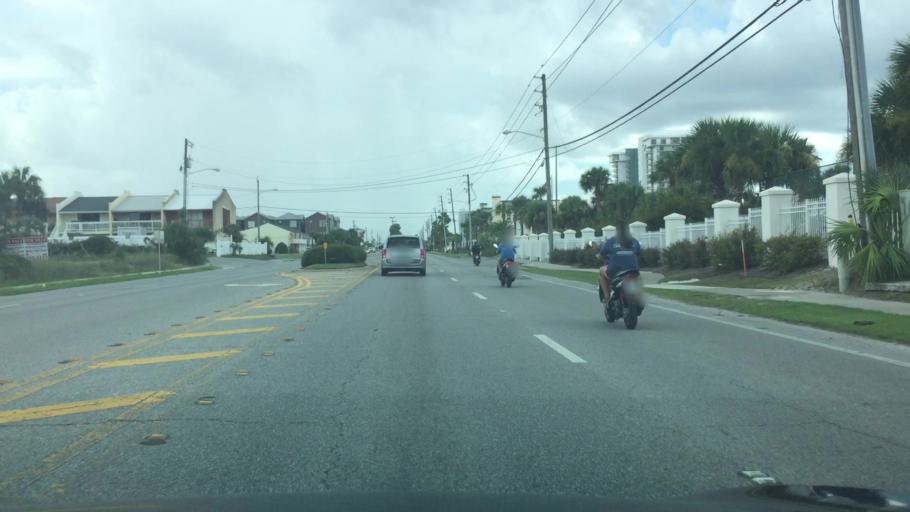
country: US
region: Florida
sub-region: Bay County
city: Lower Grand Lagoon
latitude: 30.1526
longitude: -85.7670
